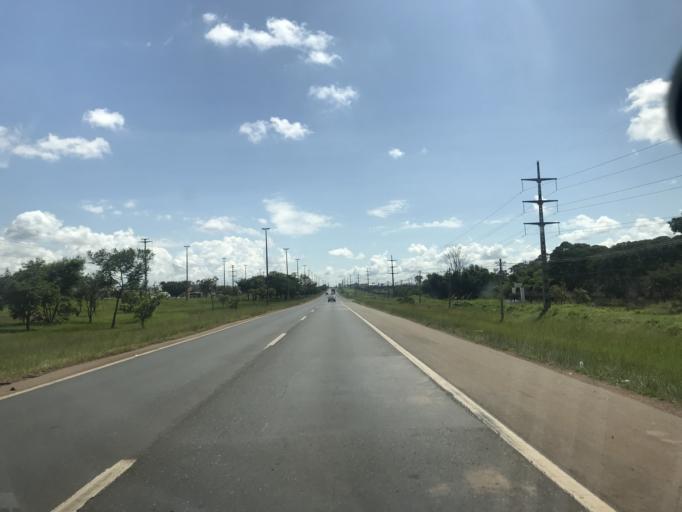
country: BR
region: Federal District
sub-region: Brasilia
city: Brasilia
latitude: -15.8877
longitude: -48.0776
